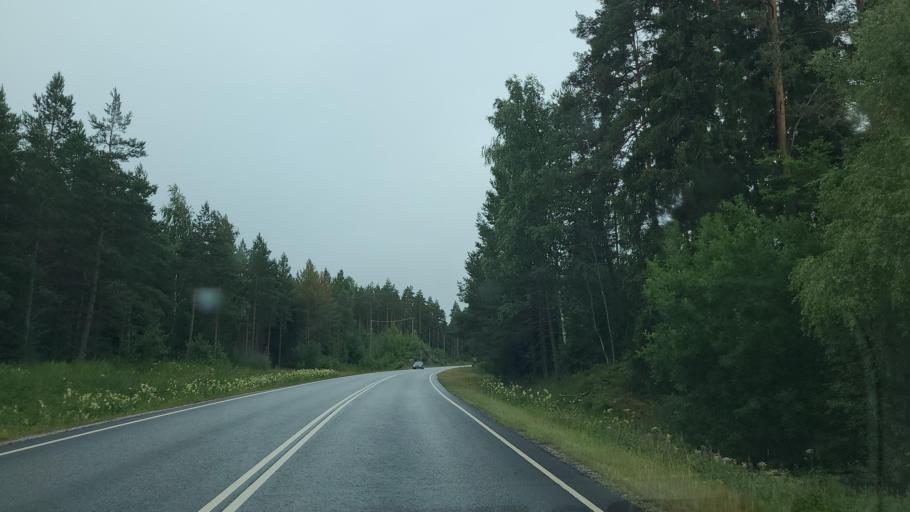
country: FI
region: Varsinais-Suomi
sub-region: Turku
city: Sauvo
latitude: 60.2725
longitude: 22.6692
